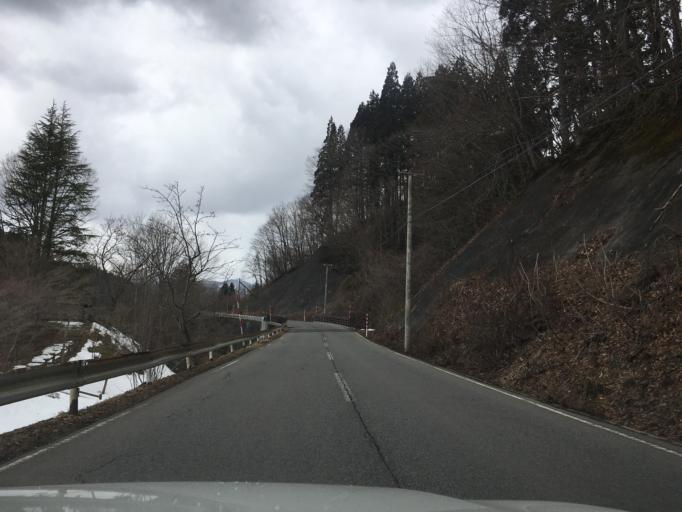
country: JP
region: Akita
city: Odate
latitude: 40.4259
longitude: 140.6556
